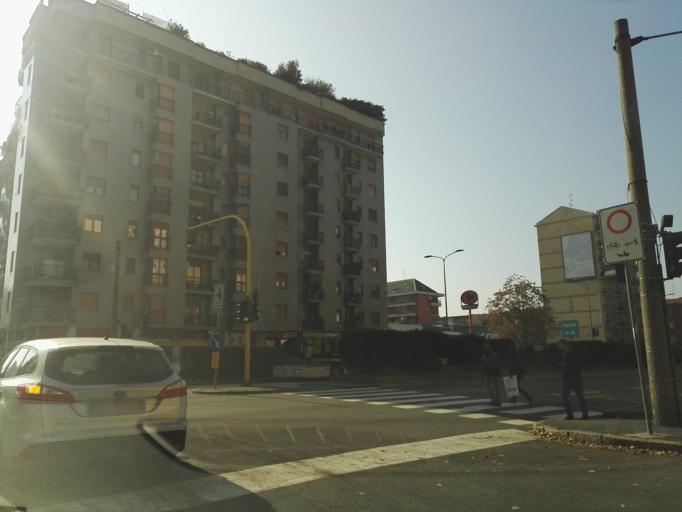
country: IT
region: Lombardy
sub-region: Citta metropolitana di Milano
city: Romano Banco
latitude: 45.4374
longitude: 9.1584
